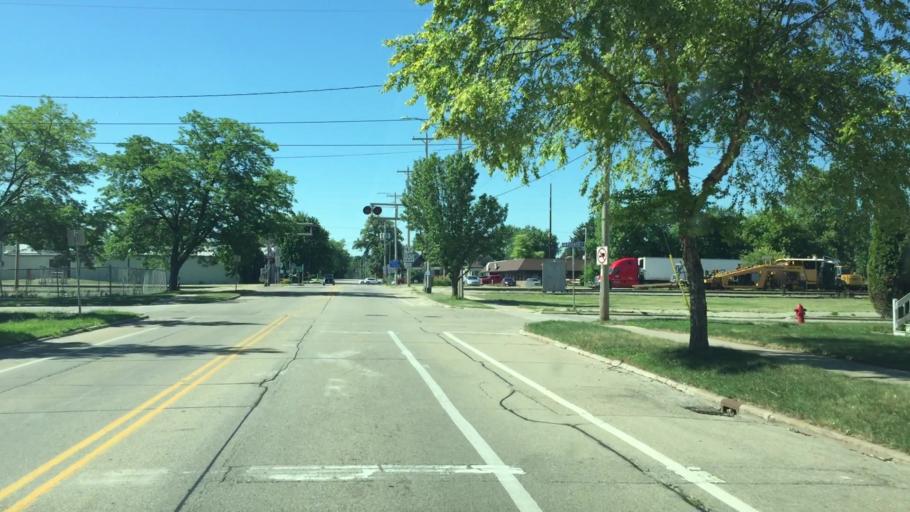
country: US
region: Wisconsin
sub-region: Winnebago County
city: Menasha
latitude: 44.2067
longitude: -88.4401
